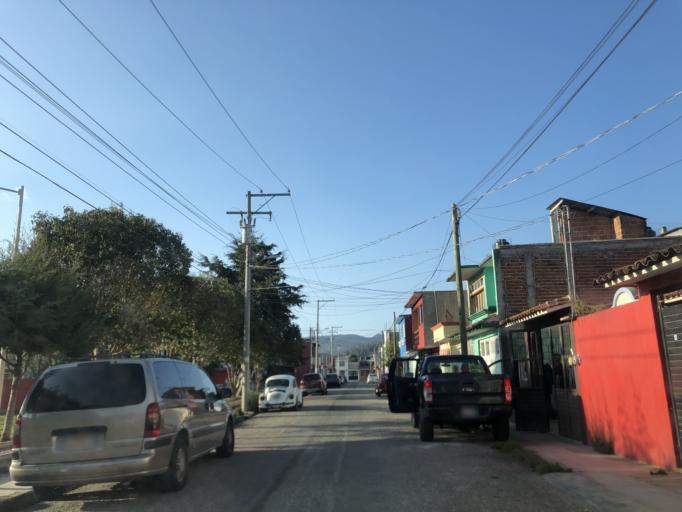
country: MX
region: Chiapas
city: San Cristobal de las Casas
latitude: 16.7166
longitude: -92.6459
